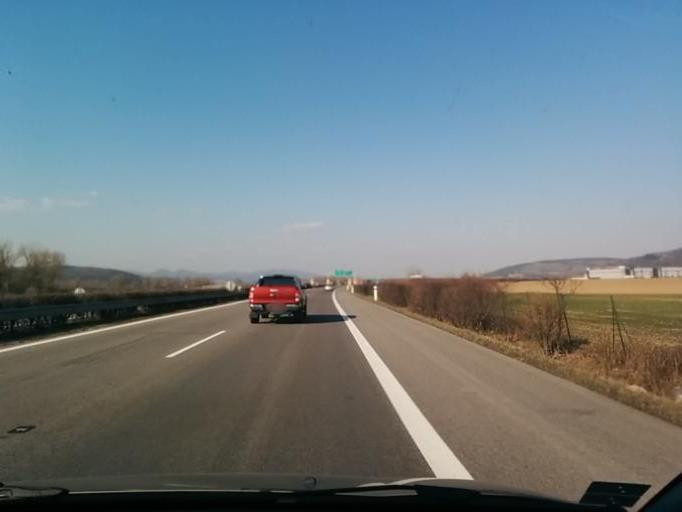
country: SK
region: Trenciansky
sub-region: Okres Nove Mesto nad Vahom
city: Nove Mesto nad Vahom
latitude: 48.7550
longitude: 17.8627
